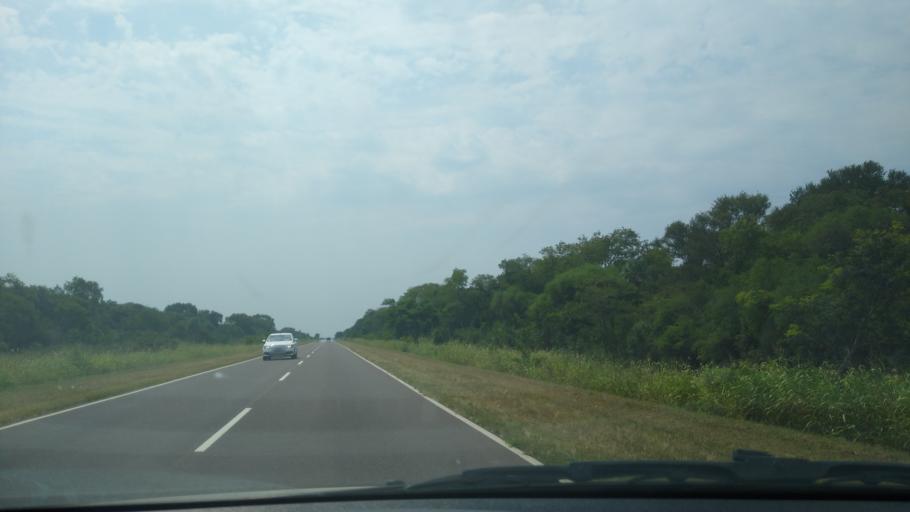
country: AR
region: Chaco
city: La Eduvigis
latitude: -27.0146
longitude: -58.9695
